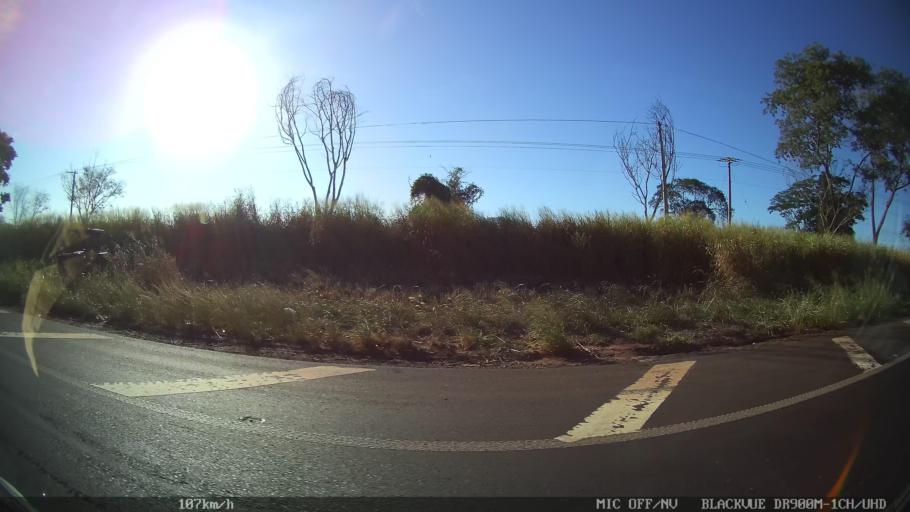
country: BR
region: Sao Paulo
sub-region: Olimpia
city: Olimpia
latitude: -20.7329
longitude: -49.0650
